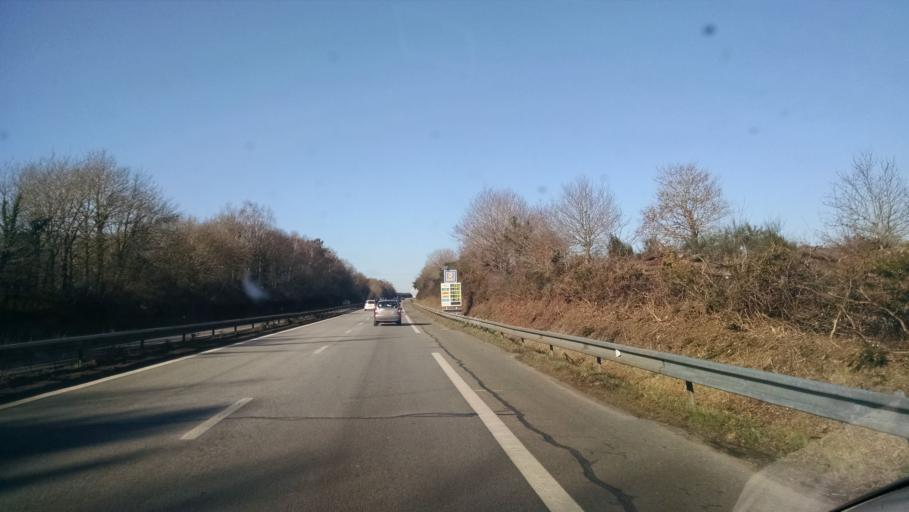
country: FR
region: Brittany
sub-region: Departement du Morbihan
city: Branderion
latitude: 47.7735
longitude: -3.1831
